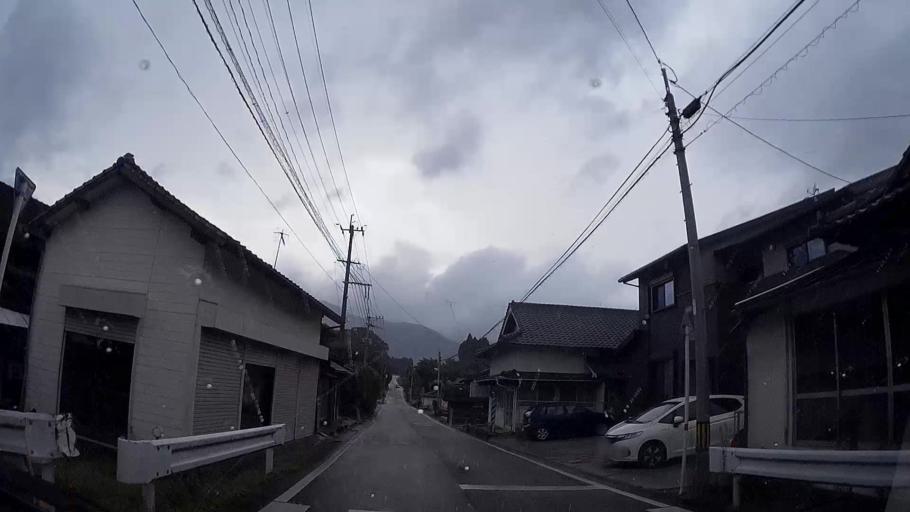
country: JP
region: Kumamoto
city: Aso
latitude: 32.8452
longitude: 131.0218
